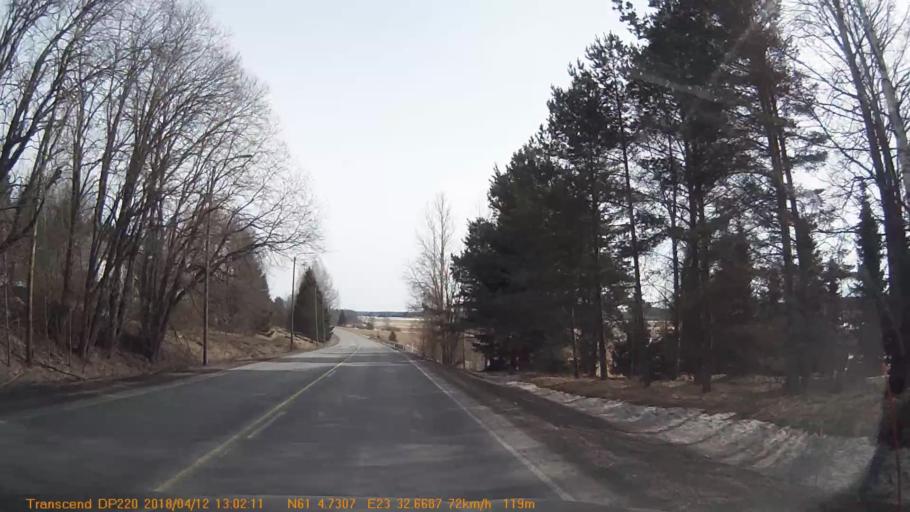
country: FI
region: Pirkanmaa
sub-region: Etelae-Pirkanmaa
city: Urjala
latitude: 61.0787
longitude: 23.5451
